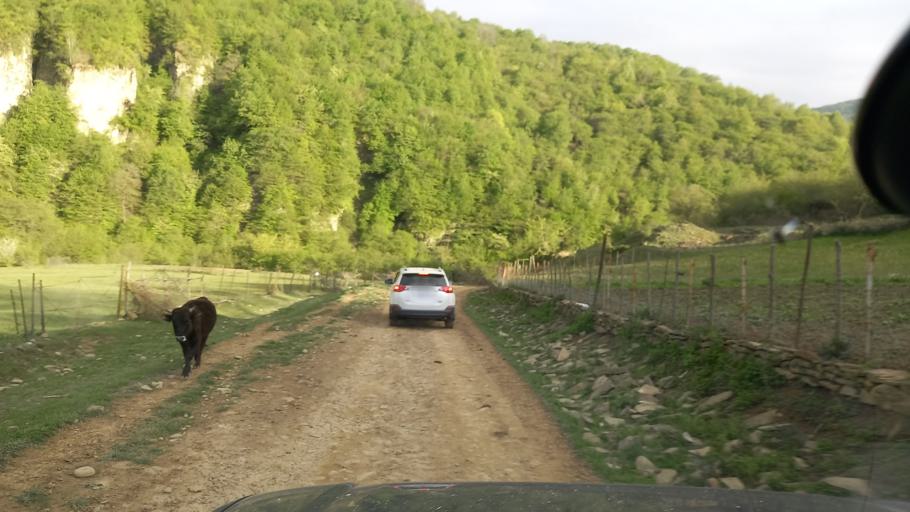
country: RU
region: Dagestan
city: Khuchni
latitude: 41.9460
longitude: 47.8346
